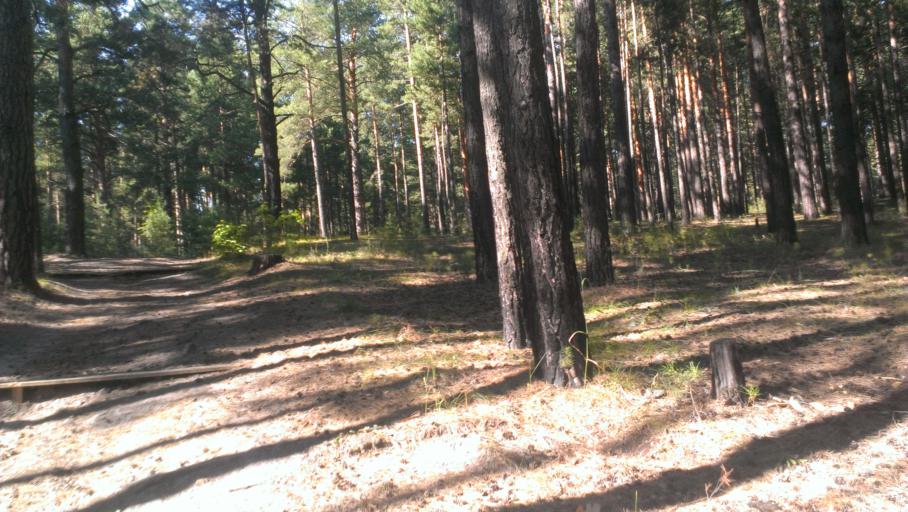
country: RU
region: Altai Krai
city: Novosilikatnyy
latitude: 53.3163
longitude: 83.6839
